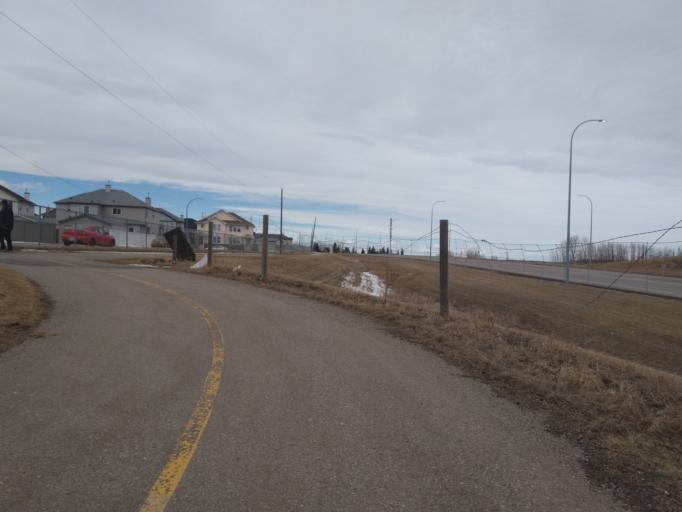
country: CA
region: Alberta
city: Chestermere
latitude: 51.1379
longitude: -113.9296
